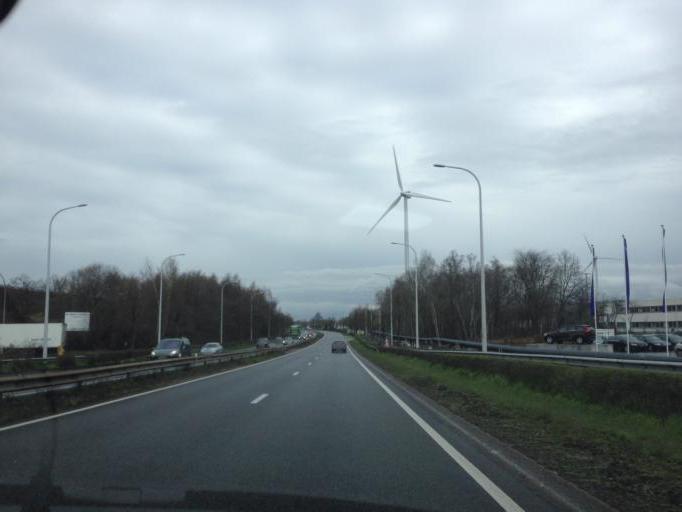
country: BE
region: Flanders
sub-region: Provincie Limburg
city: Genk
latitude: 50.9392
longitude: 5.4722
